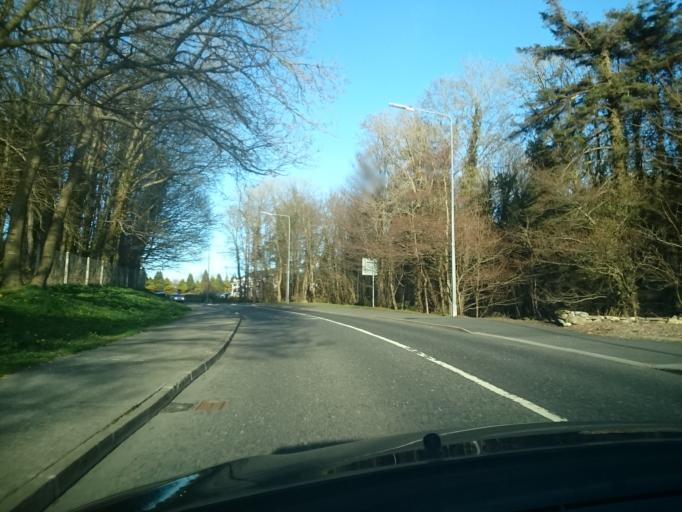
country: IE
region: Connaught
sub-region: Maigh Eo
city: Westport
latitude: 53.8062
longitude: -9.5301
